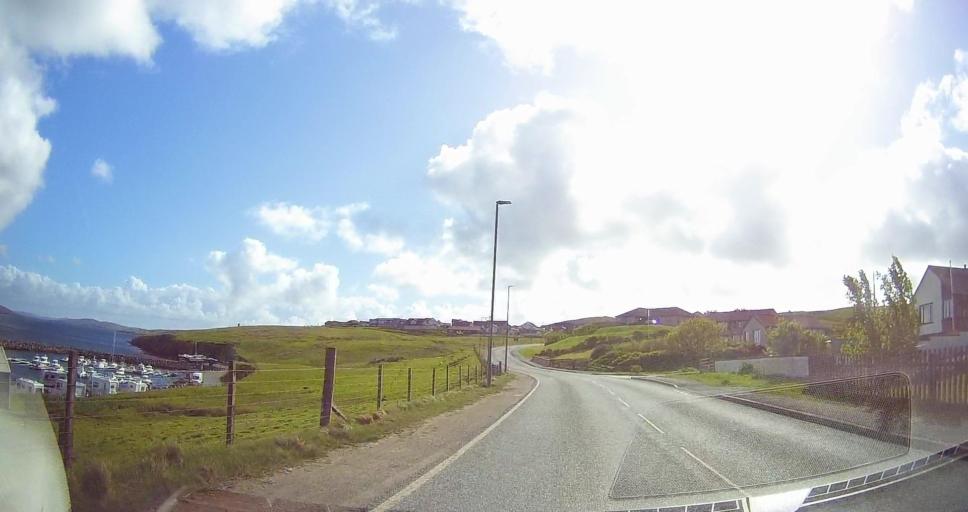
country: GB
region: Scotland
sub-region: Shetland Islands
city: Lerwick
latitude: 60.3933
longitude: -1.3649
